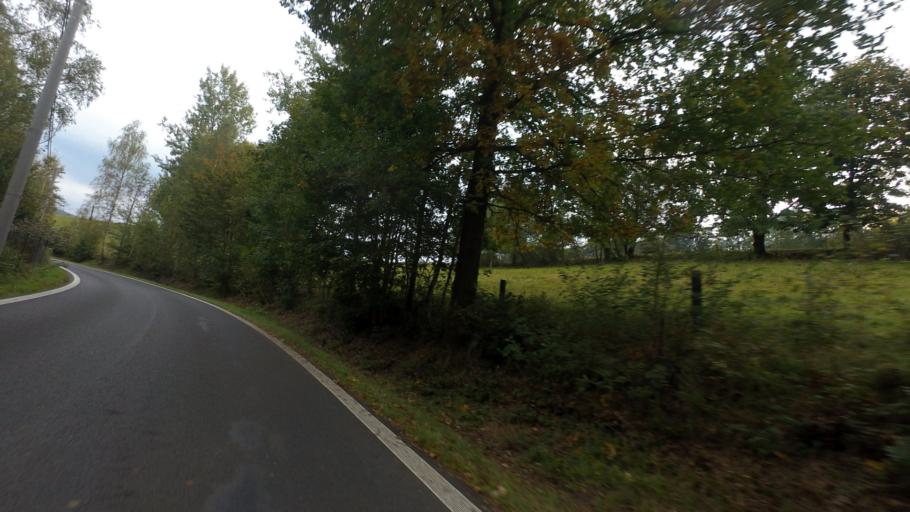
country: CZ
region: Ustecky
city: Dolni Poustevna
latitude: 51.0054
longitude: 14.2944
